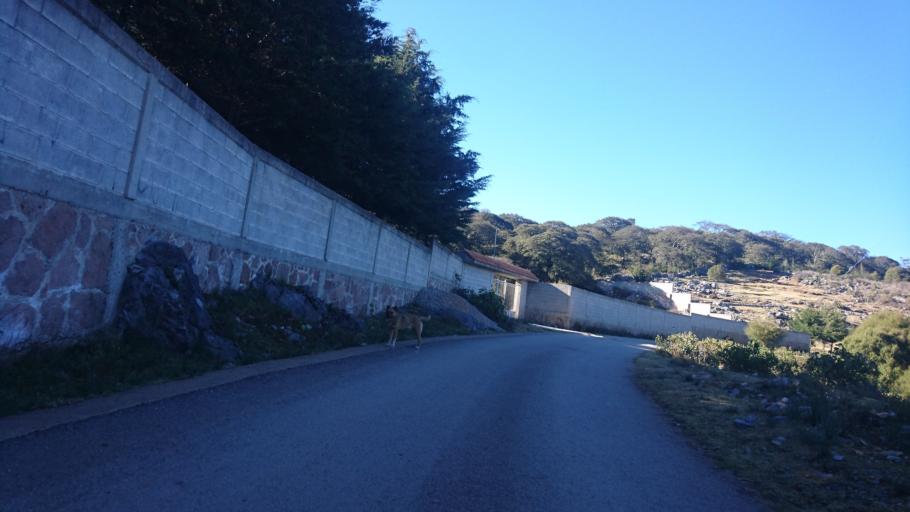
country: MX
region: San Luis Potosi
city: Zaragoza
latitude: 22.0236
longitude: -100.6027
